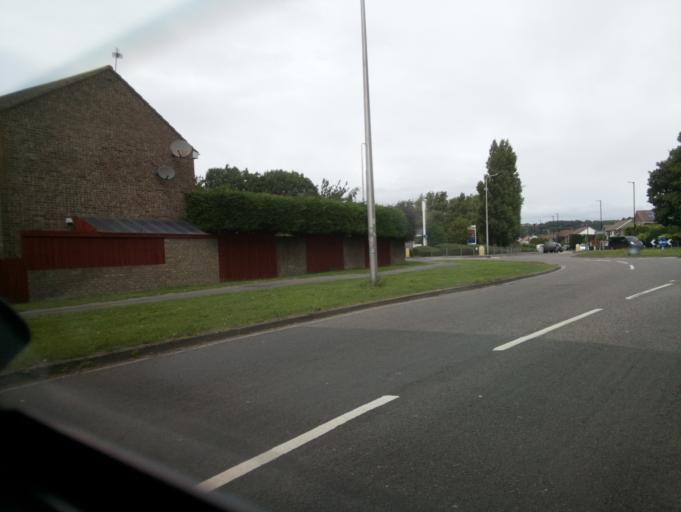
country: GB
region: England
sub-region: North Somerset
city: Kenn
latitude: 51.4268
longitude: -2.8538
